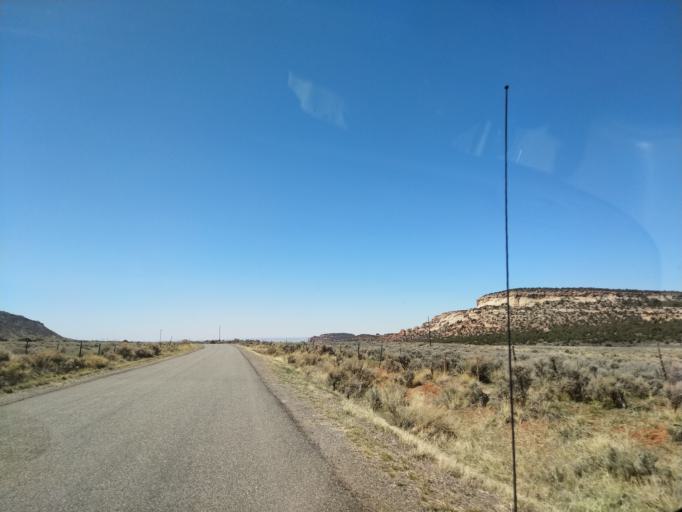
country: US
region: Colorado
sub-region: Mesa County
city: Loma
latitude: 38.9578
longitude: -109.0175
